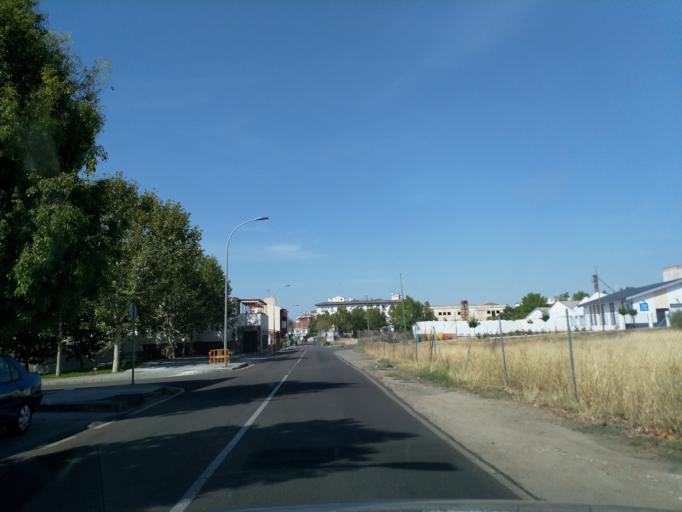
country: ES
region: Extremadura
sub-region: Provincia de Badajoz
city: Merida
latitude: 38.9253
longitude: -6.3453
